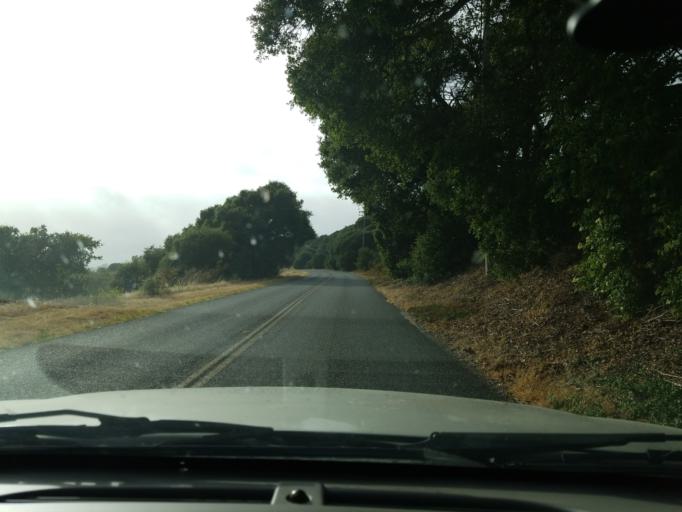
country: US
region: California
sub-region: Monterey County
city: Elkhorn
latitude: 36.8417
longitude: -121.7396
